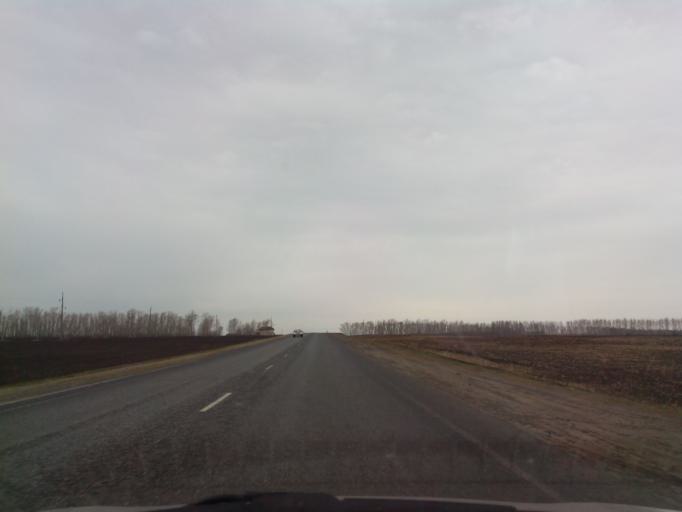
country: RU
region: Tambov
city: Zavoronezhskoye
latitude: 52.9825
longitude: 40.5631
